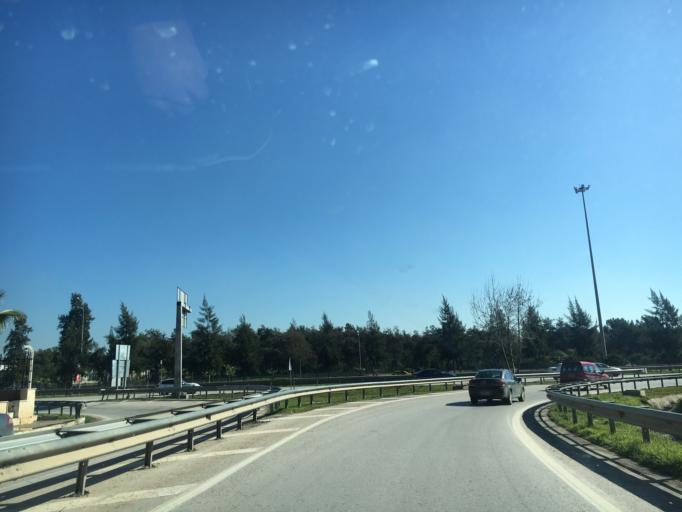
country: TR
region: Antalya
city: Antalya
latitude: 36.9026
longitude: 30.6639
